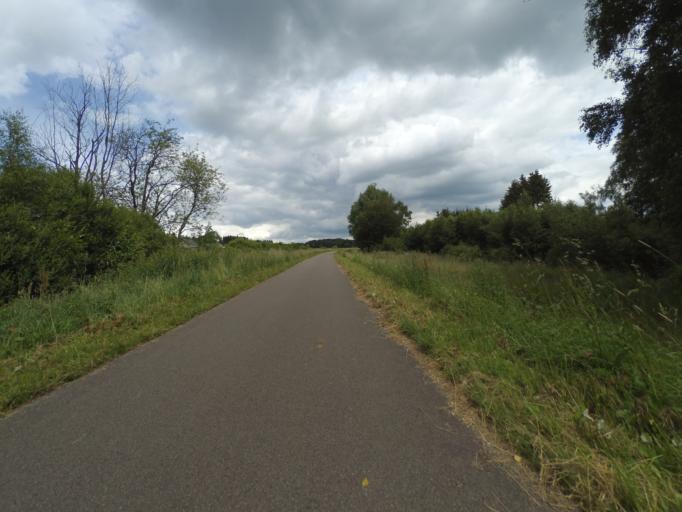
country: DE
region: North Rhine-Westphalia
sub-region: Regierungsbezirk Koln
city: Monschau
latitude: 50.5848
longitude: 6.2396
